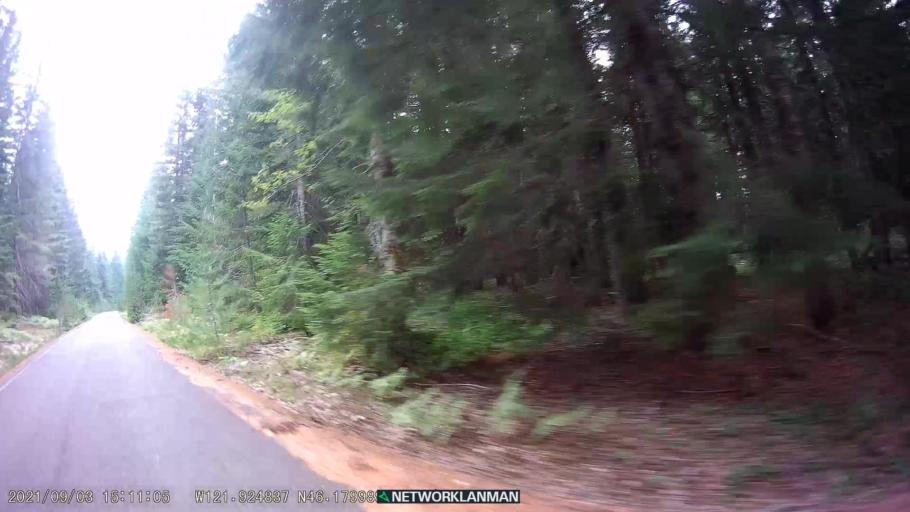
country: US
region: Washington
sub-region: Skamania County
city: Carson
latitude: 46.1798
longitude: -121.9249
